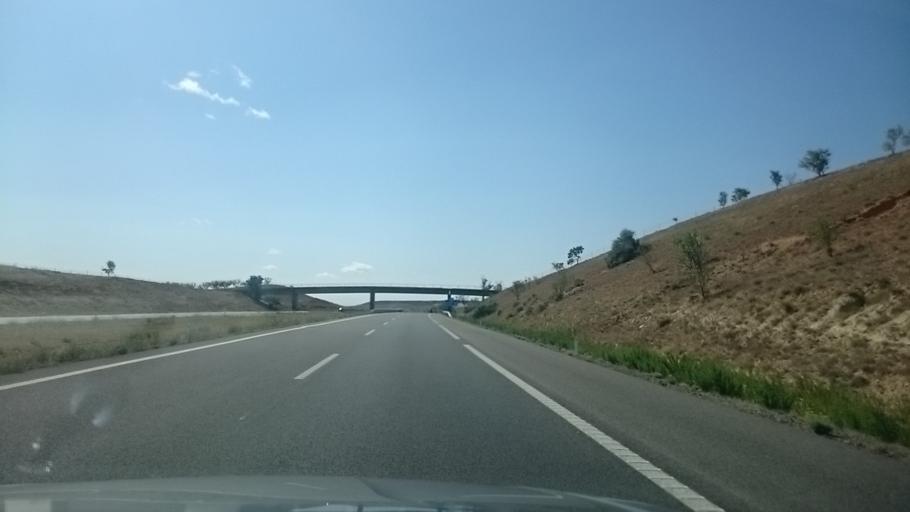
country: ES
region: Navarre
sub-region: Provincia de Navarra
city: Ribaforada
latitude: 41.9735
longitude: -1.5485
